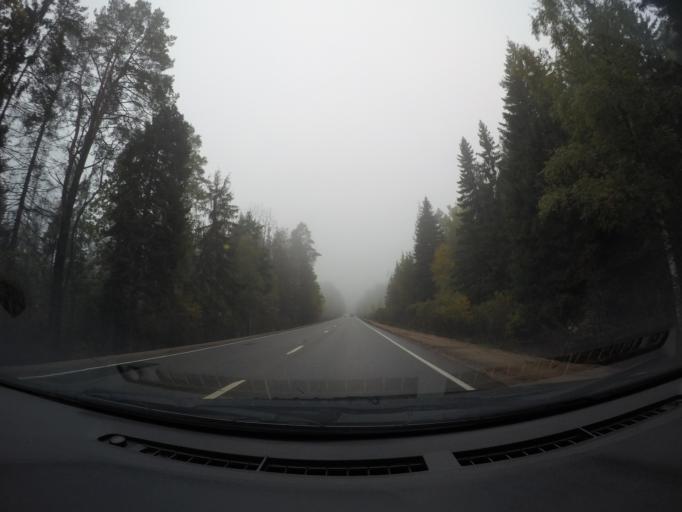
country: RU
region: Moskovskaya
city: Ruza
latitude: 55.7176
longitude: 36.2715
